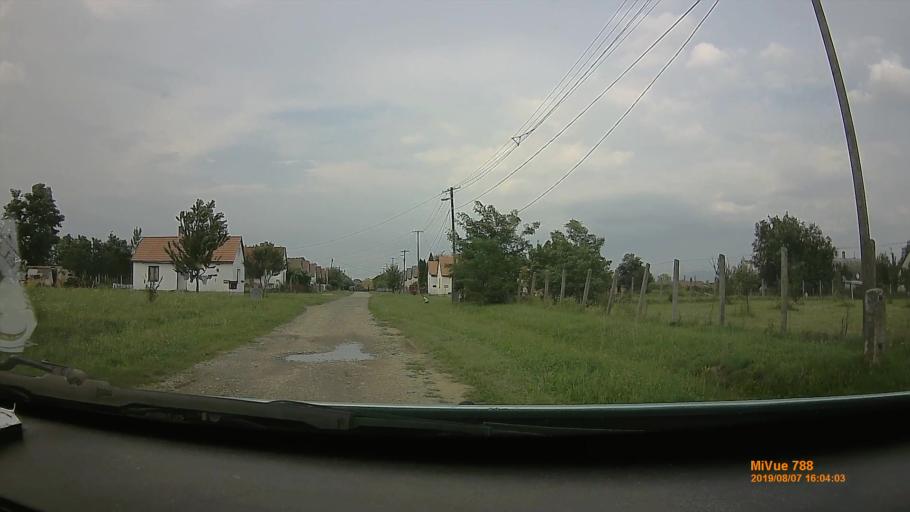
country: HU
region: Borsod-Abauj-Zemplen
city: Gonc
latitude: 48.4993
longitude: 21.2240
